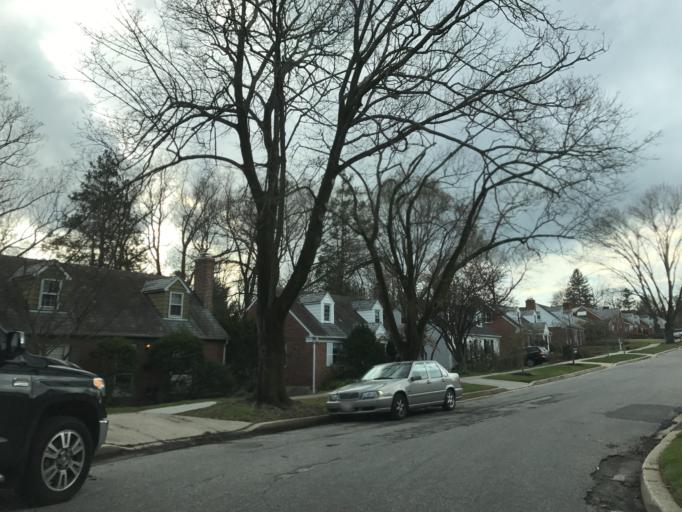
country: US
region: Maryland
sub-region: Baltimore County
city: Lutherville
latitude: 39.4024
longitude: -76.6219
